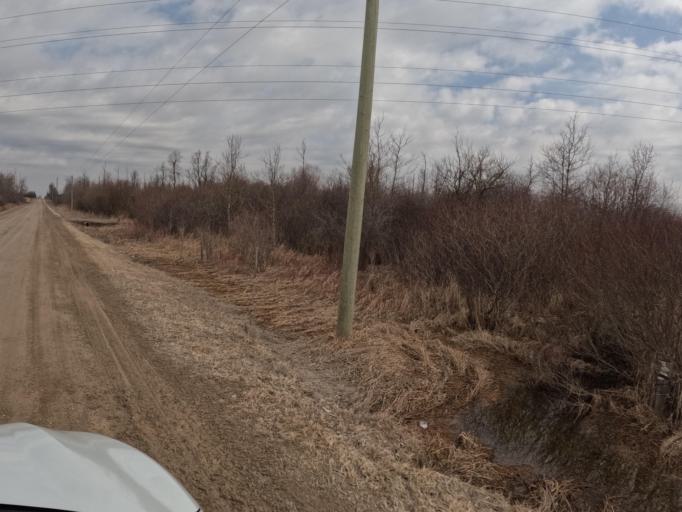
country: CA
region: Ontario
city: Orangeville
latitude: 43.9348
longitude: -80.2212
